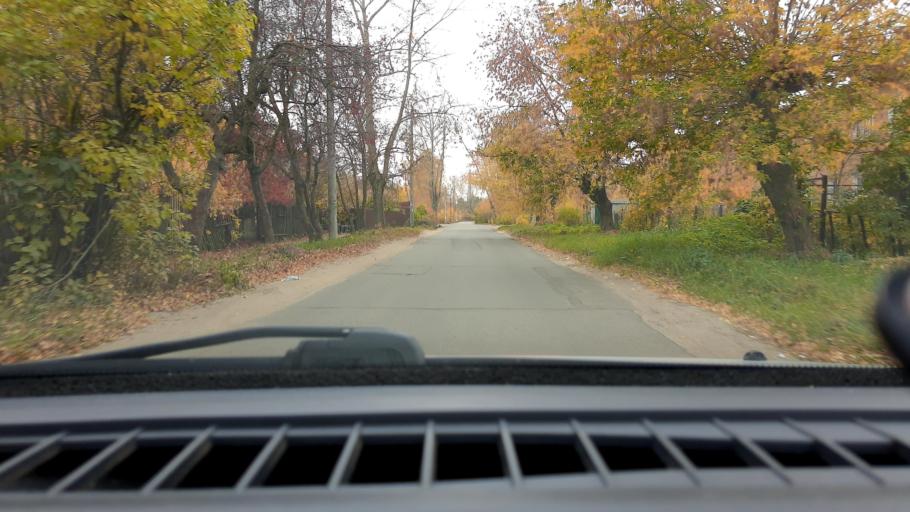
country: RU
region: Nizjnij Novgorod
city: Gorbatovka
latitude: 56.3810
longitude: 43.7926
